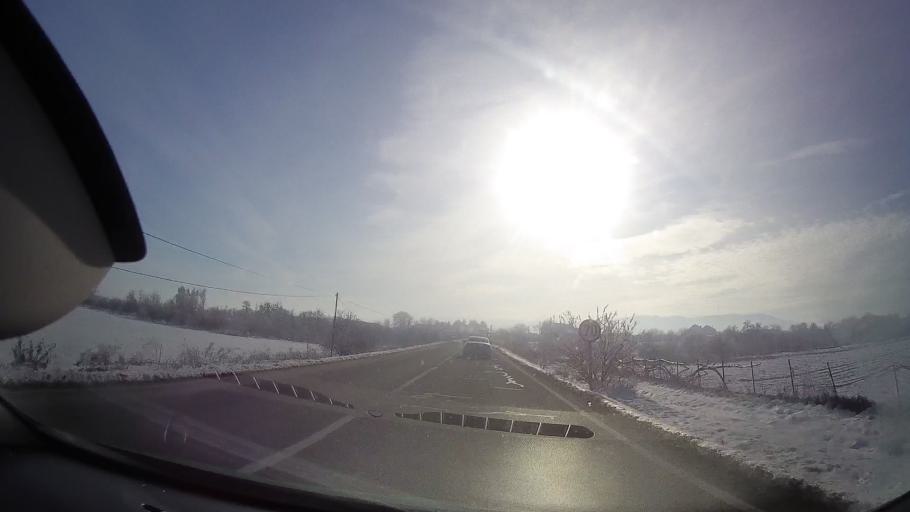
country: RO
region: Neamt
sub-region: Comuna Dobreni
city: Dobreni
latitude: 47.0044
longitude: 26.4239
